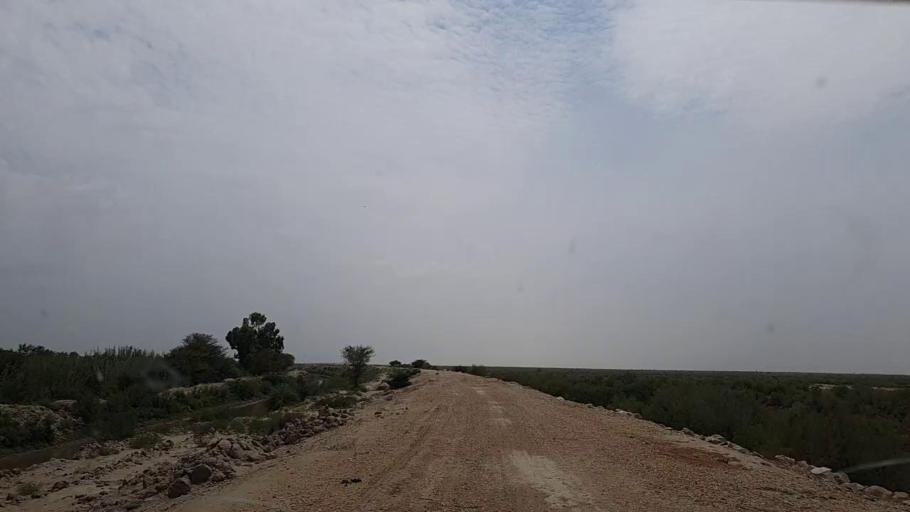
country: PK
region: Sindh
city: Phulji
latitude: 26.8475
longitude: 67.6199
